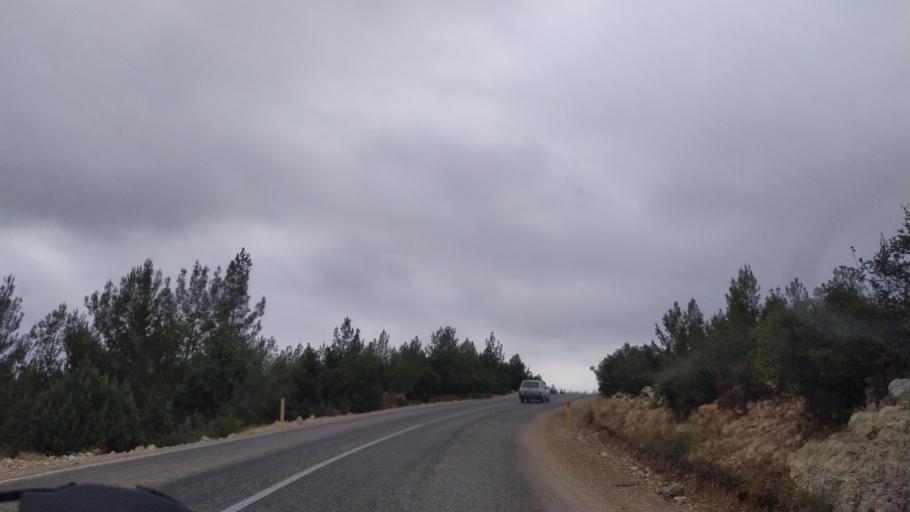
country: TR
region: Mersin
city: Silifke
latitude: 36.5407
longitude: 33.9290
